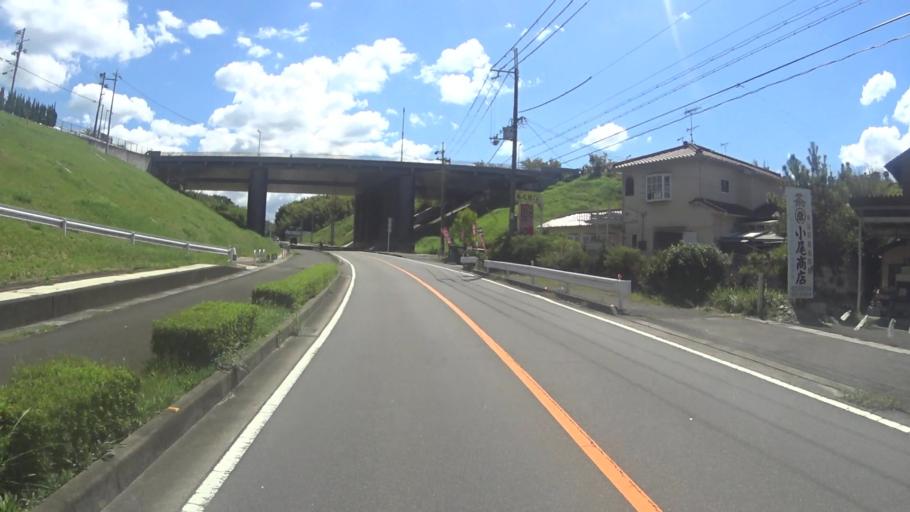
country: JP
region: Nara
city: Nara-shi
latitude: 34.7168
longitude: 135.8265
